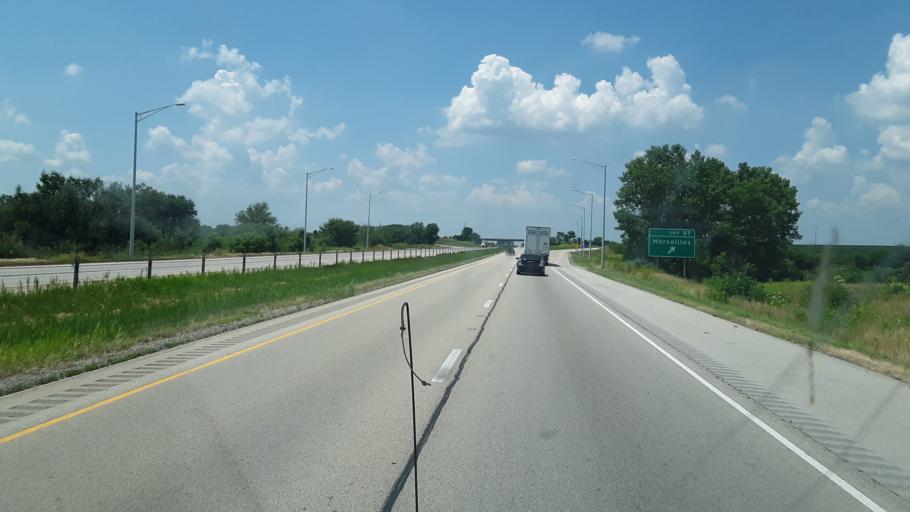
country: US
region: Illinois
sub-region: LaSalle County
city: Marseilles
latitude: 41.3755
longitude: -88.6974
